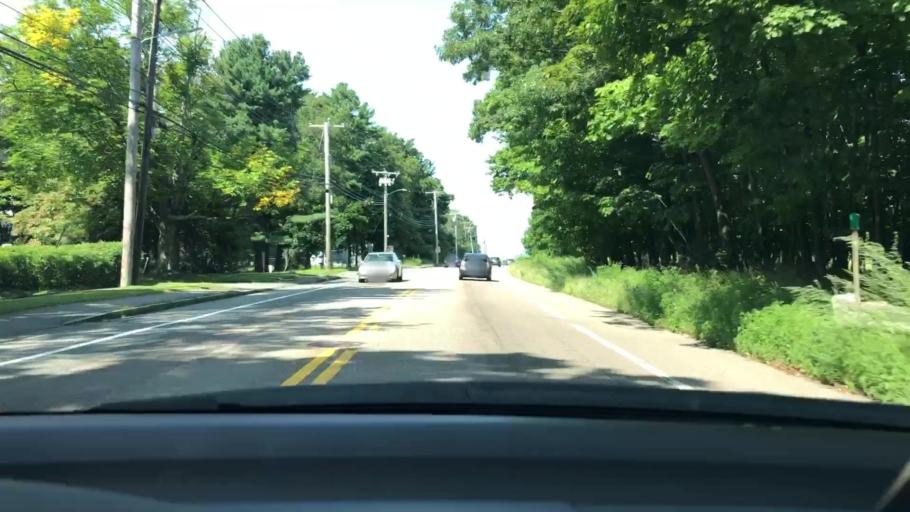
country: US
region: Massachusetts
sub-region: Norfolk County
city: Canton
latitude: 42.1968
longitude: -71.1191
